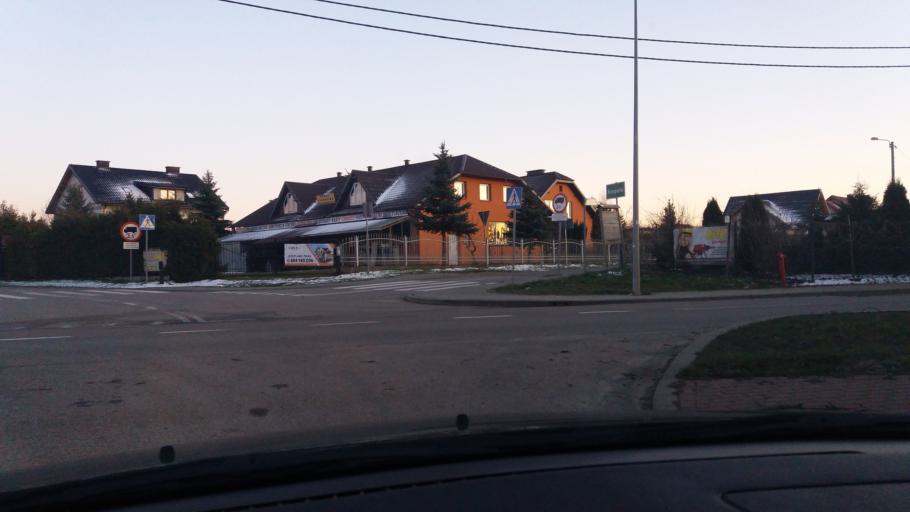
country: PL
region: Warmian-Masurian Voivodeship
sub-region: Powiat szczycienski
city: Szczytno
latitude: 53.5615
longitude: 20.9664
